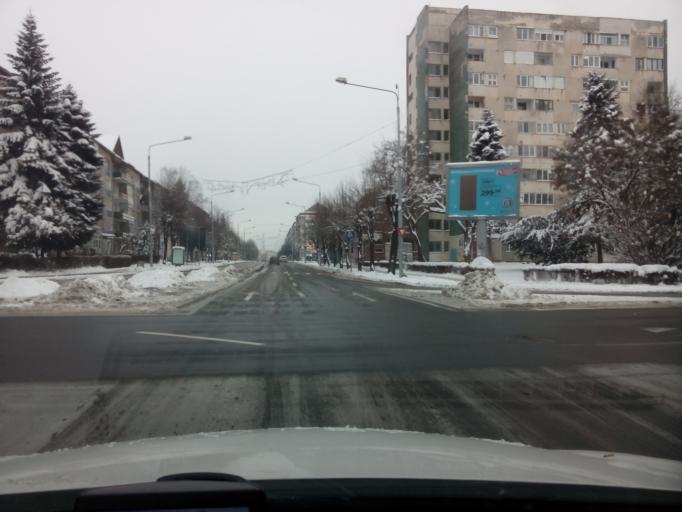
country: RO
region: Sibiu
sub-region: Municipiul Sibiu
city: Sibiu
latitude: 45.7893
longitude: 24.1500
